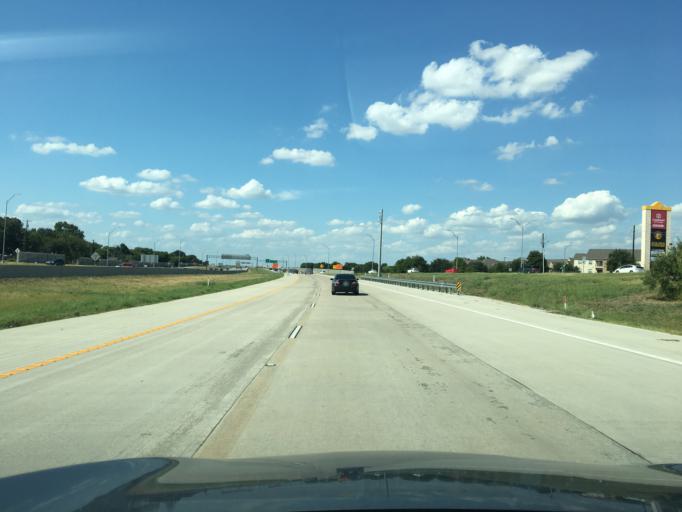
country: US
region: Texas
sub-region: Tarrant County
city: Arlington
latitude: 32.6501
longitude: -97.0616
